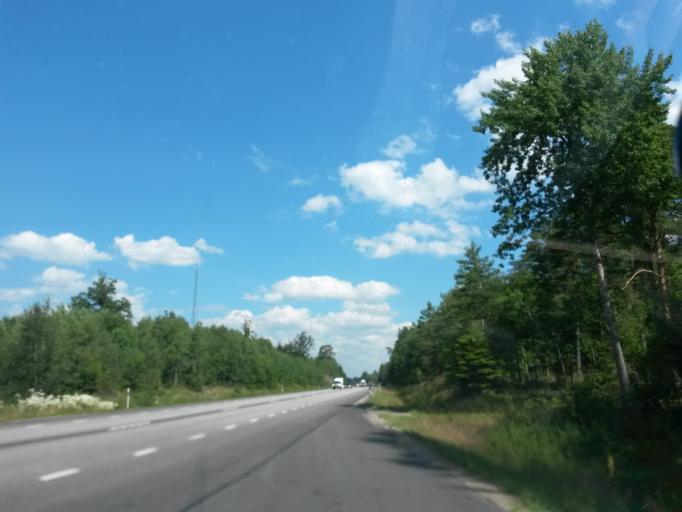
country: SE
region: Vaestra Goetaland
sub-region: Vargarda Kommun
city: Vargarda
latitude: 58.1227
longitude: 12.8514
